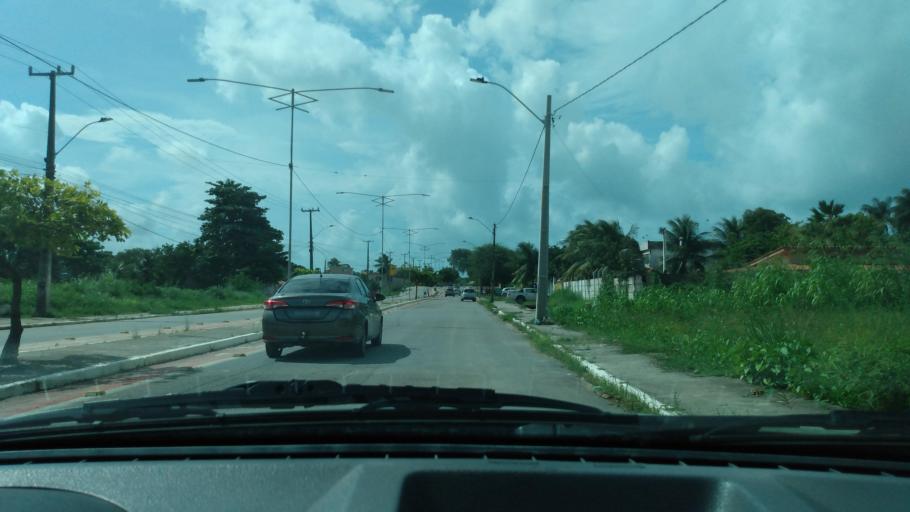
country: BR
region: Pernambuco
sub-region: Cabo De Santo Agostinho
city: Cabo
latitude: -8.3141
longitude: -34.9493
